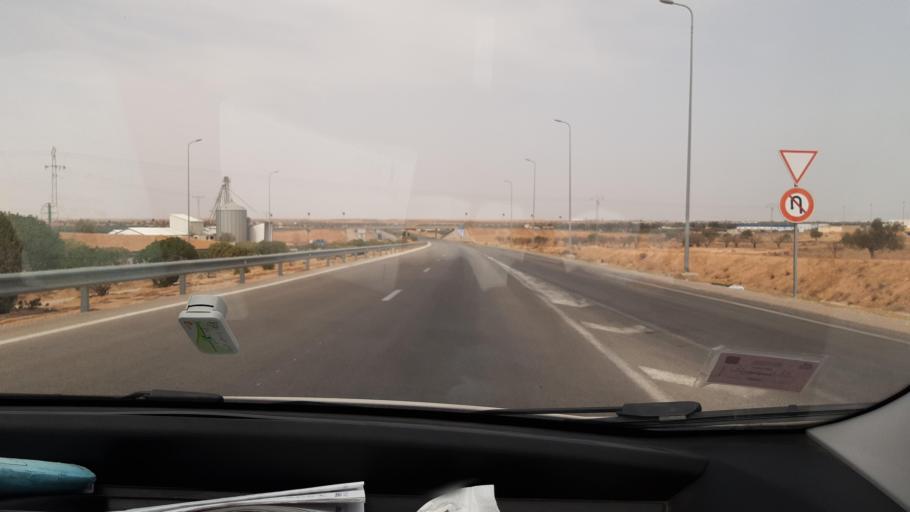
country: TN
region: Safaqis
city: Sfax
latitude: 34.7286
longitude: 10.5902
